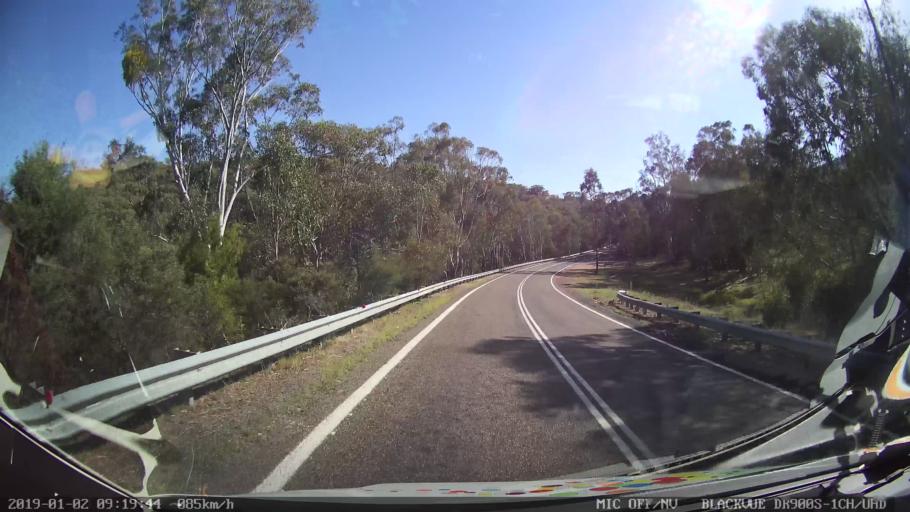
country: AU
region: New South Wales
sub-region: Tumut Shire
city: Tumut
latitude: -35.4188
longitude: 148.2768
